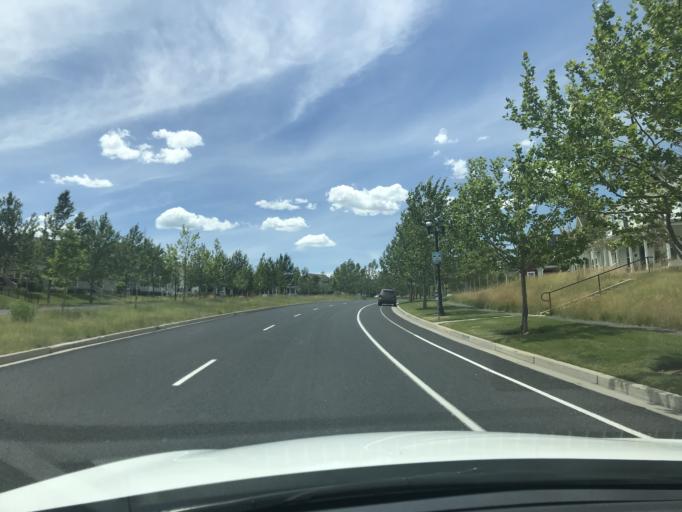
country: US
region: Utah
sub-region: Salt Lake County
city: South Jordan Heights
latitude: 40.5602
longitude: -111.9932
